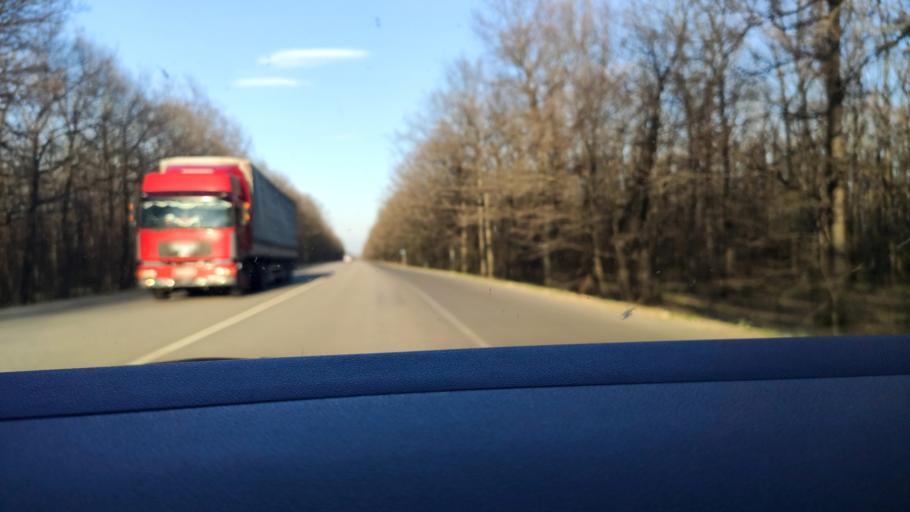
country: RU
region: Voronezj
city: Kolodeznyy
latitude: 51.3388
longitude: 39.0589
